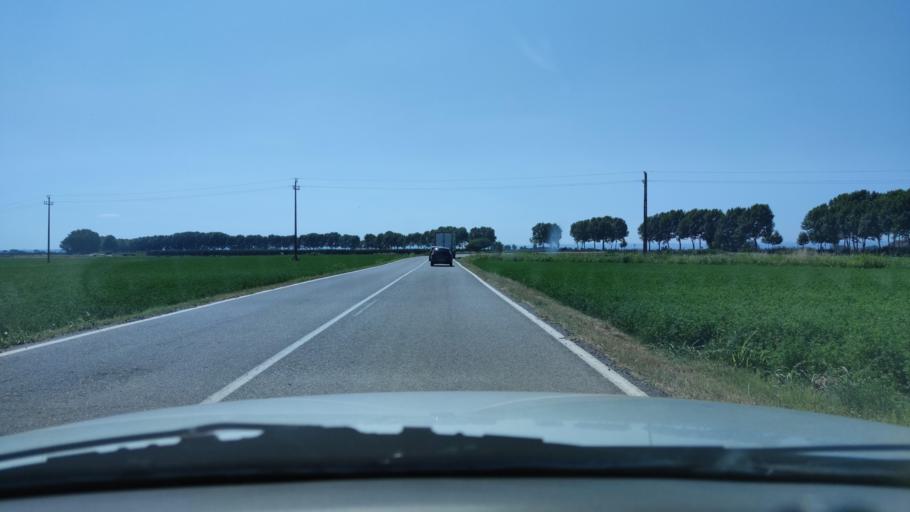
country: ES
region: Catalonia
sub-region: Provincia de Lleida
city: Ivars d'Urgell
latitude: 41.6925
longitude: 0.9877
